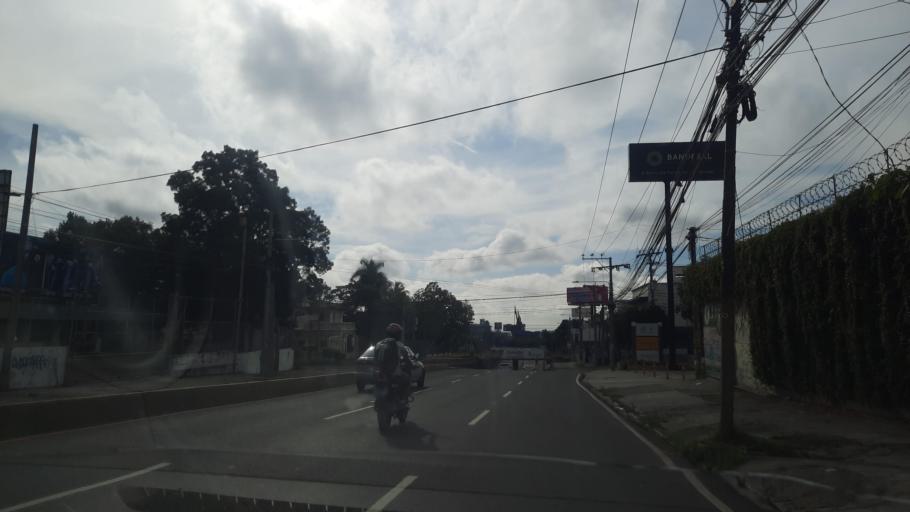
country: SV
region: San Salvador
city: San Salvador
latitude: 13.7006
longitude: -89.2179
